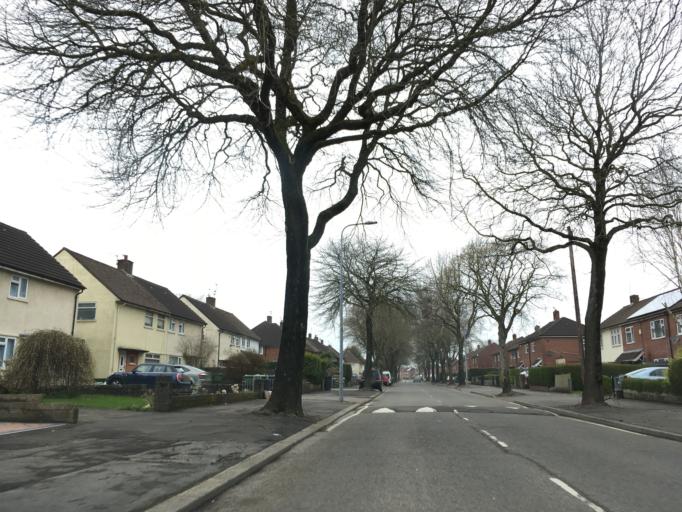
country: GB
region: Wales
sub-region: Cardiff
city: Cardiff
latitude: 51.5024
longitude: -3.2086
